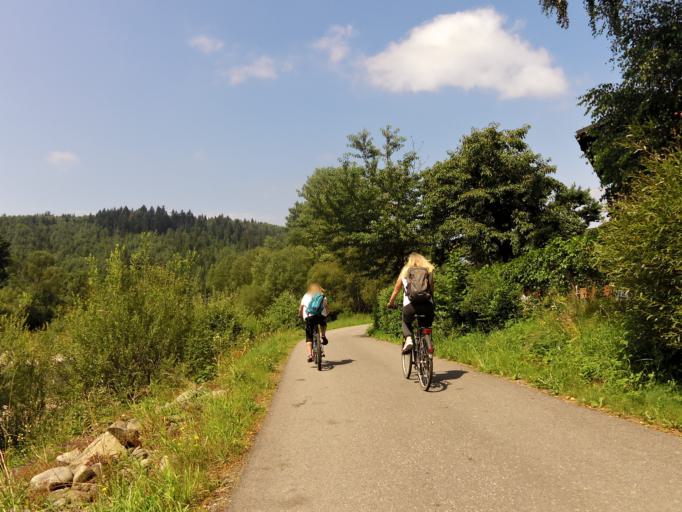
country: PL
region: Silesian Voivodeship
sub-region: Powiat zywiecki
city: Rajcza
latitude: 49.5251
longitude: 19.1106
